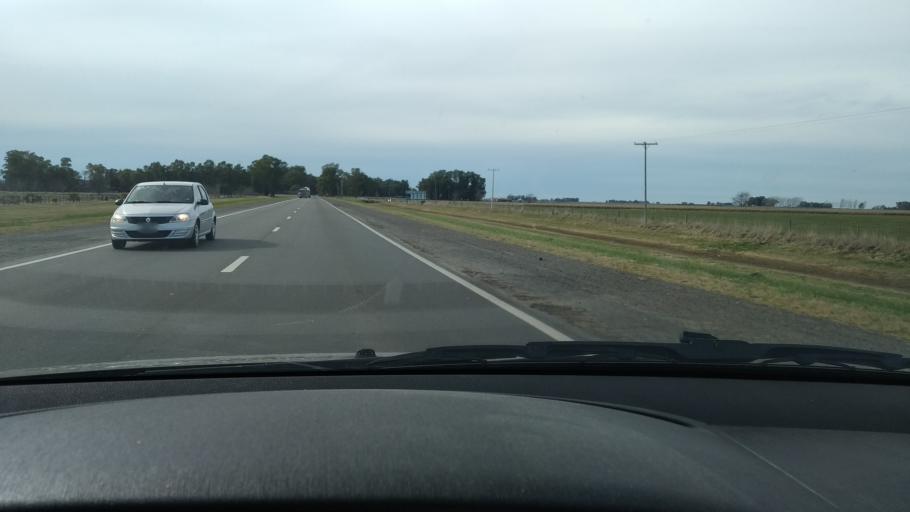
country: AR
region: Buenos Aires
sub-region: Partido de Azul
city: Azul
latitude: -36.7675
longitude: -59.8114
